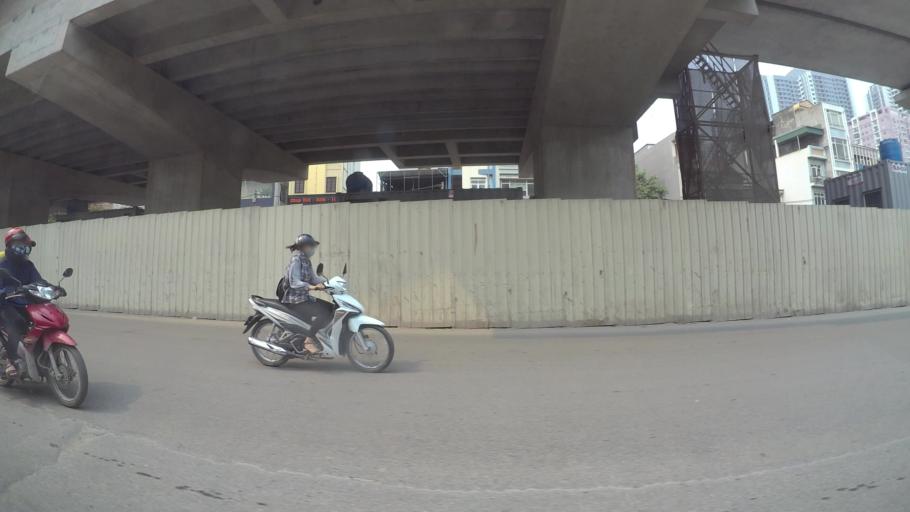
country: VN
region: Ha Noi
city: Cau Dien
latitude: 21.0409
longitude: 105.7632
